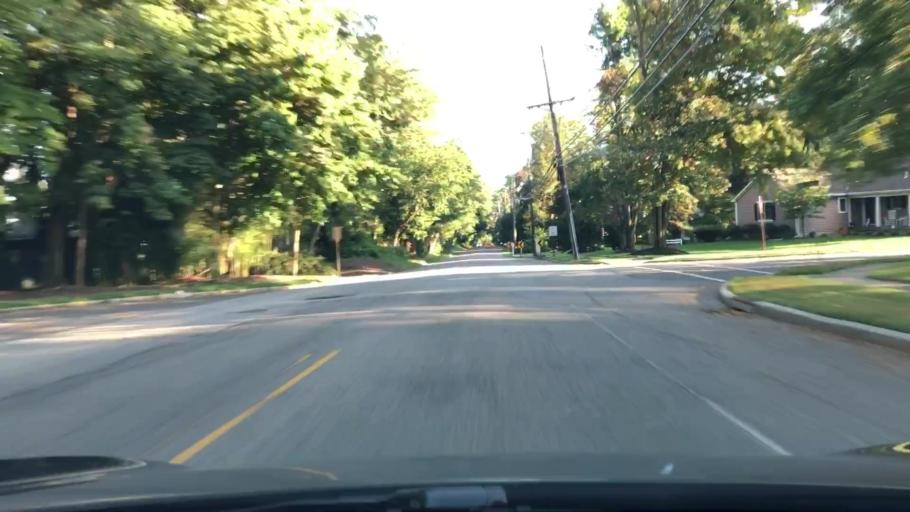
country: US
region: New Jersey
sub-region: Mercer County
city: Lawrenceville
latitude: 40.3056
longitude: -74.7295
